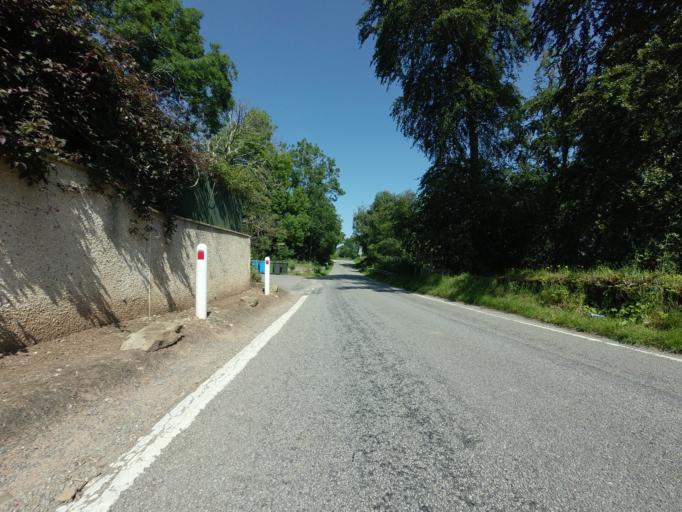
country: GB
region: Scotland
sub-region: Highland
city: Dingwall
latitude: 57.6107
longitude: -4.4178
